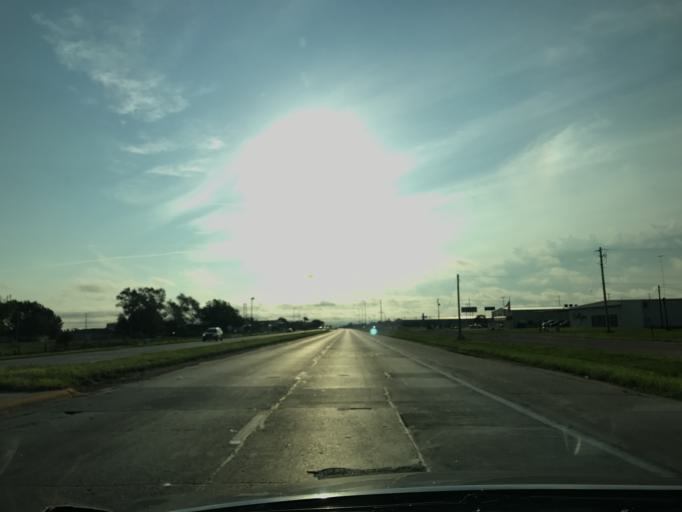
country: US
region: Nebraska
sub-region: Platte County
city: Columbus
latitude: 41.4384
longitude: -97.3145
